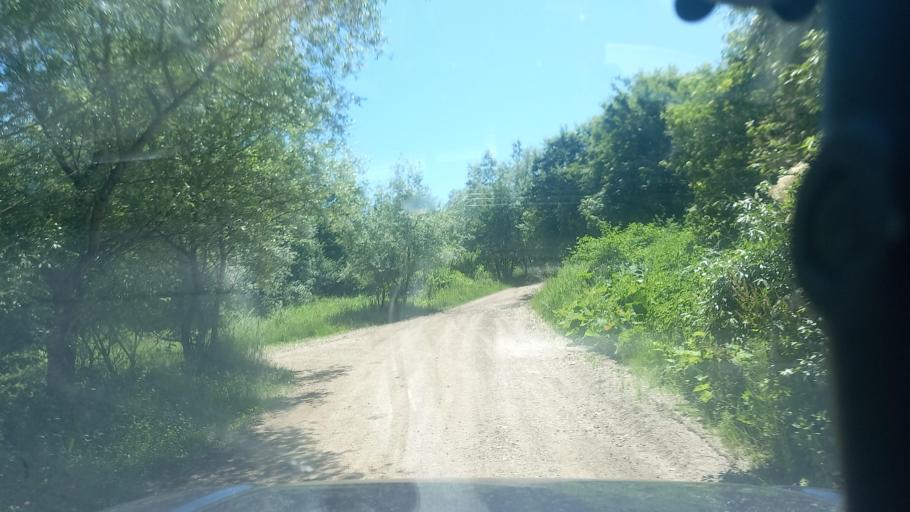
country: RU
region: Karachayevo-Cherkesiya
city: Pregradnaya
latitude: 44.1147
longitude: 41.1026
